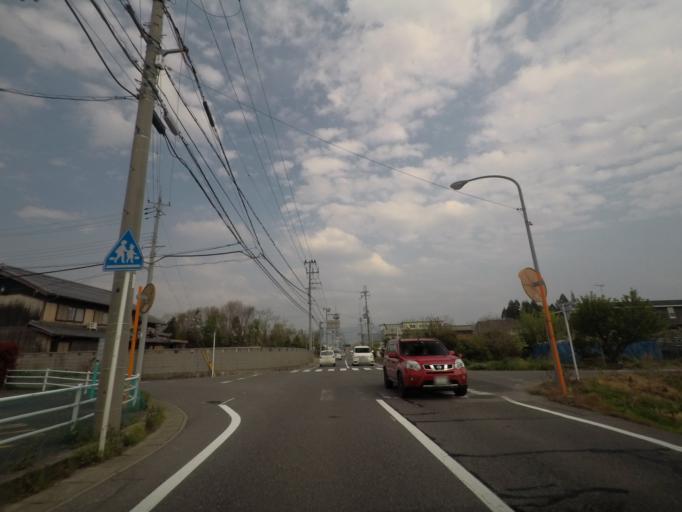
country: JP
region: Shiga Prefecture
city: Youkaichi
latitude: 35.0880
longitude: 136.2521
